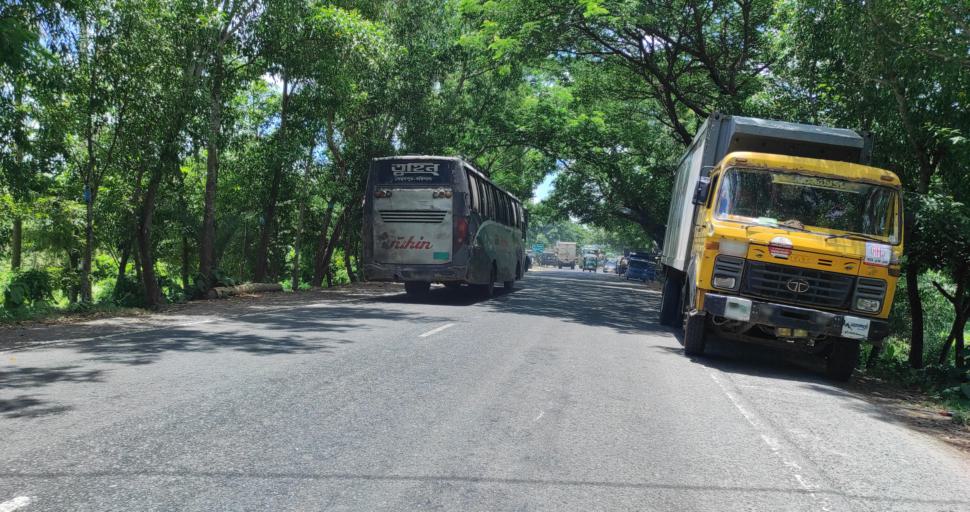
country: BD
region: Barisal
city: Gaurnadi
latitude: 22.8323
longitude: 90.2557
